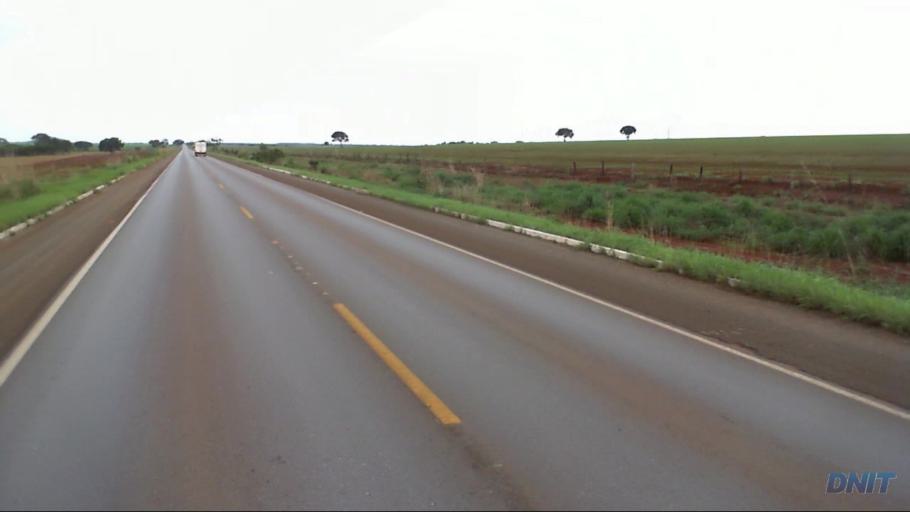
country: BR
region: Goias
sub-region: Barro Alto
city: Barro Alto
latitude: -14.8263
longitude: -49.0367
